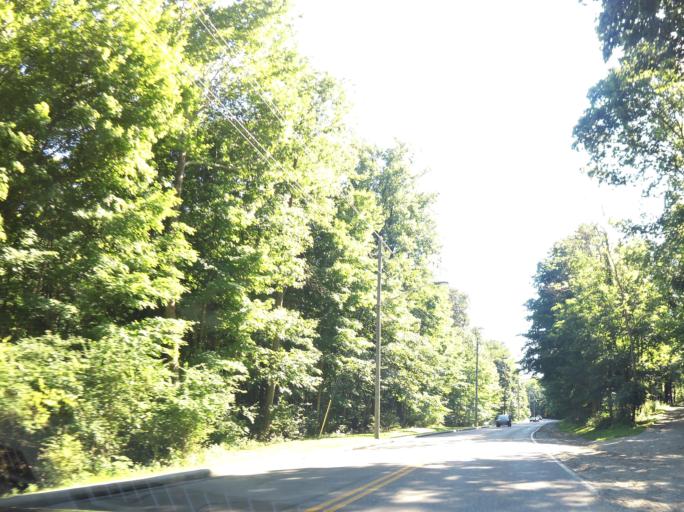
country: US
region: Ohio
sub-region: Greene County
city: Wright-Patterson AFB
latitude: 39.7871
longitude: -84.0568
